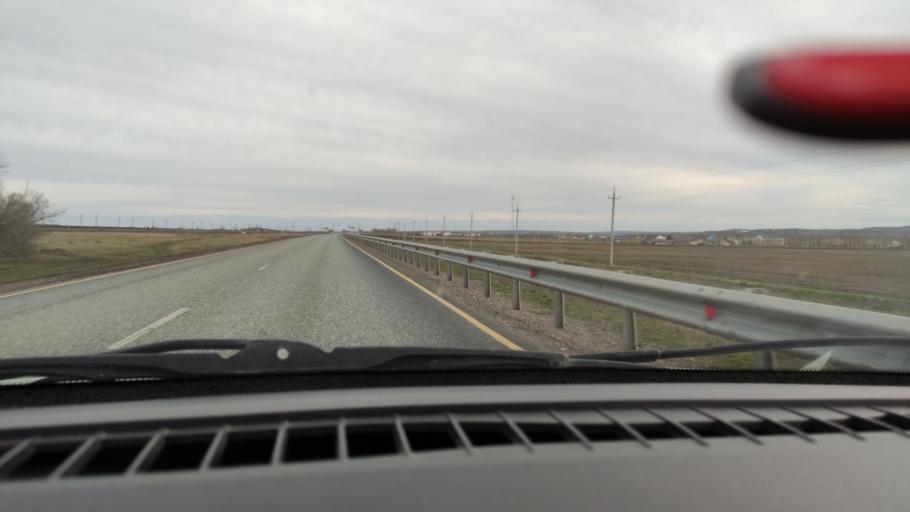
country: RU
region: Bashkortostan
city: Yermolayevo
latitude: 52.4953
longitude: 55.8289
